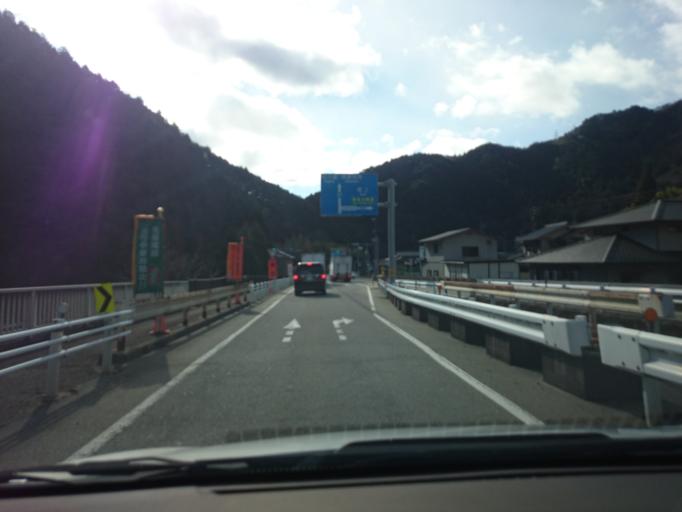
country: JP
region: Gifu
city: Gujo
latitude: 35.7482
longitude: 137.2100
